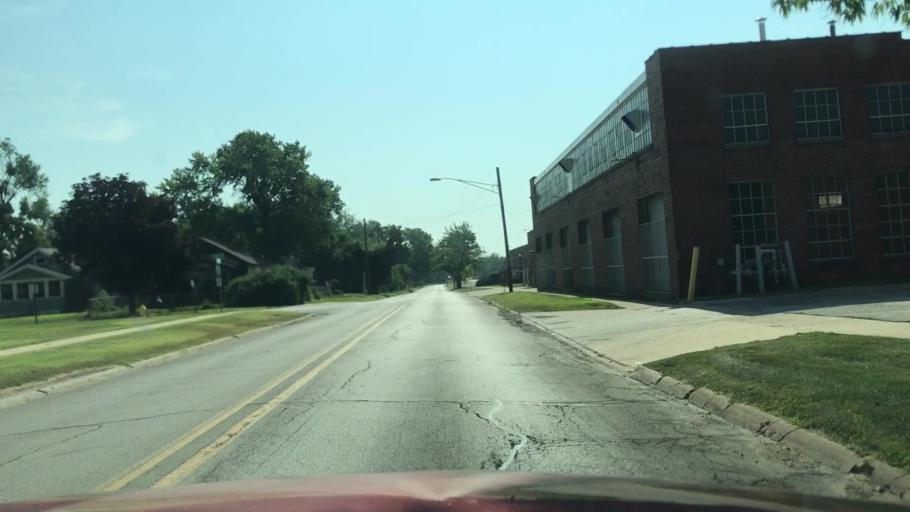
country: US
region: Illinois
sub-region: Winnebago County
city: Rockford
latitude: 42.2411
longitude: -89.0818
